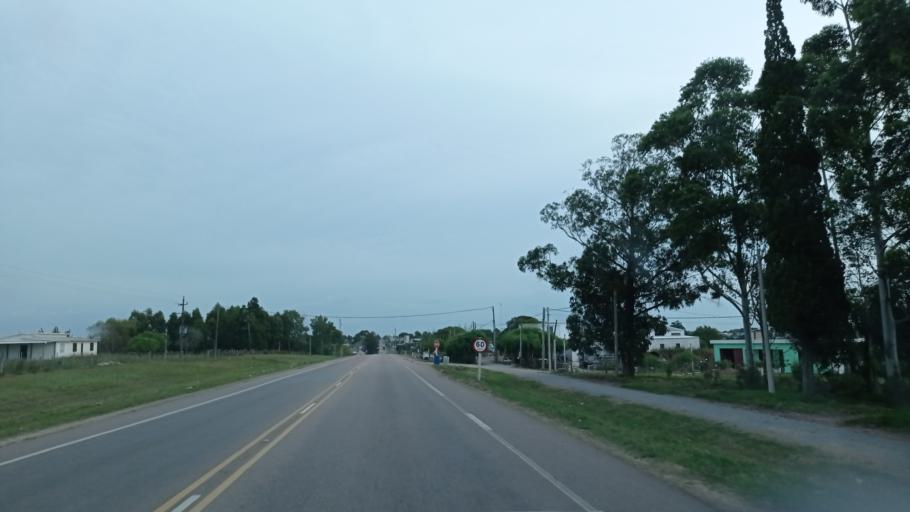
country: UY
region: Canelones
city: San Jacinto
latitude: -34.5375
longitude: -55.8601
